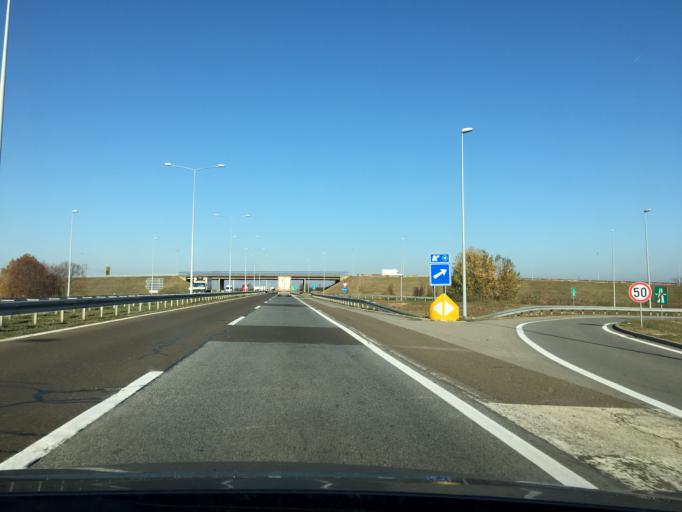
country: RS
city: Novi Karlovci
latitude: 45.0703
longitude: 20.1513
